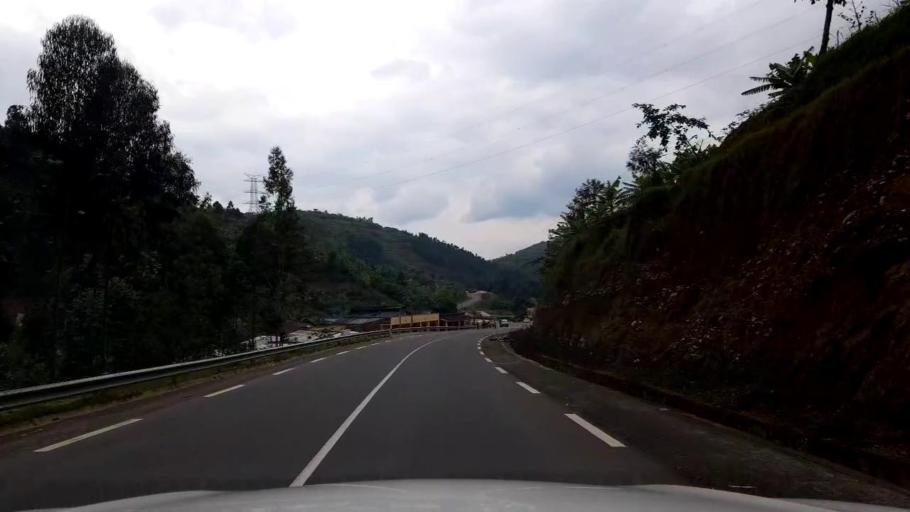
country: RW
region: Western Province
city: Kibuye
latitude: -1.9134
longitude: 29.3690
